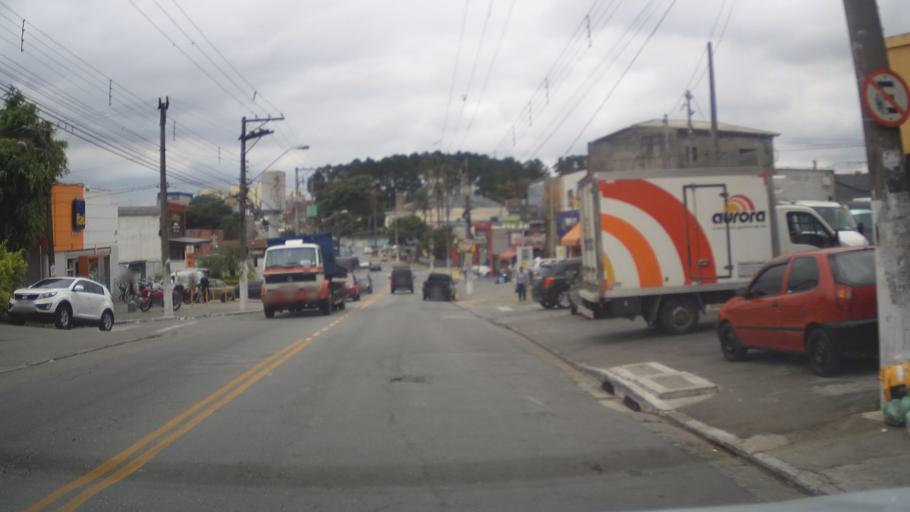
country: BR
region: Sao Paulo
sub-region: Itaquaquecetuba
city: Itaquaquecetuba
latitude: -23.4593
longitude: -46.4114
